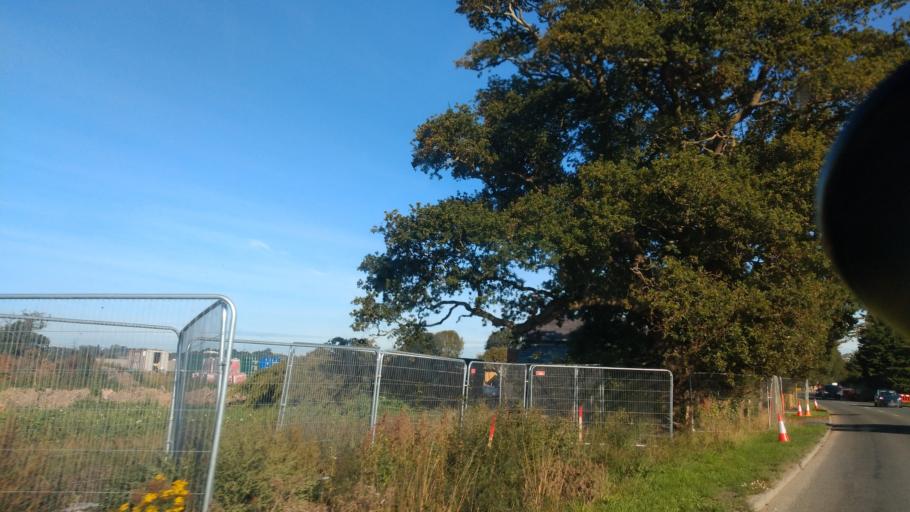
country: GB
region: England
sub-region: Hampshire
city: Lee-on-the-Solent
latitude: 50.8414
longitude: -1.2266
